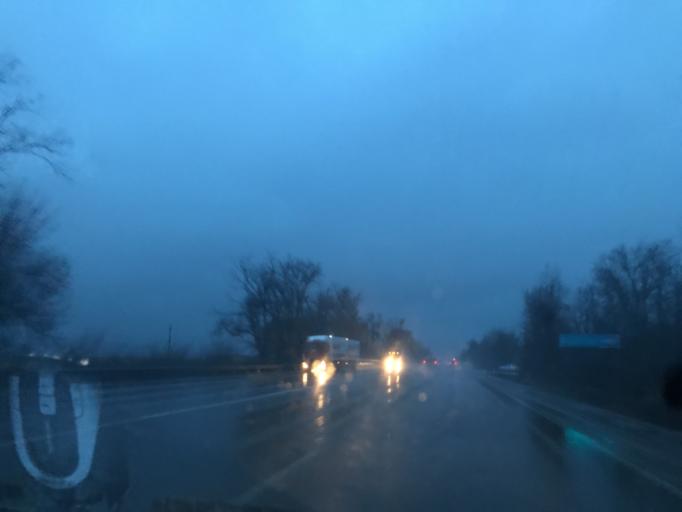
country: RU
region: Rostov
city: Bataysk
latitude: 47.0535
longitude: 39.7442
